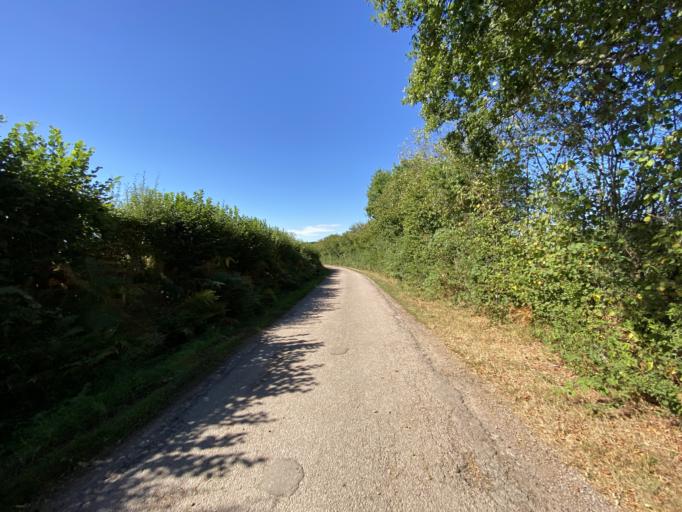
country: FR
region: Bourgogne
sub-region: Departement de la Cote-d'Or
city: Saulieu
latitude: 47.2805
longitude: 4.1805
